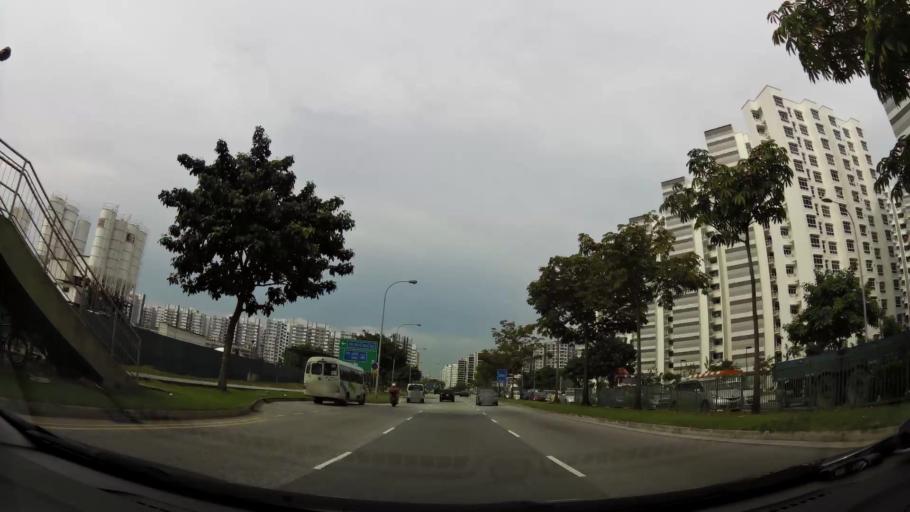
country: MY
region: Johor
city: Kampung Pasir Gudang Baru
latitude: 1.3977
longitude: 103.8951
